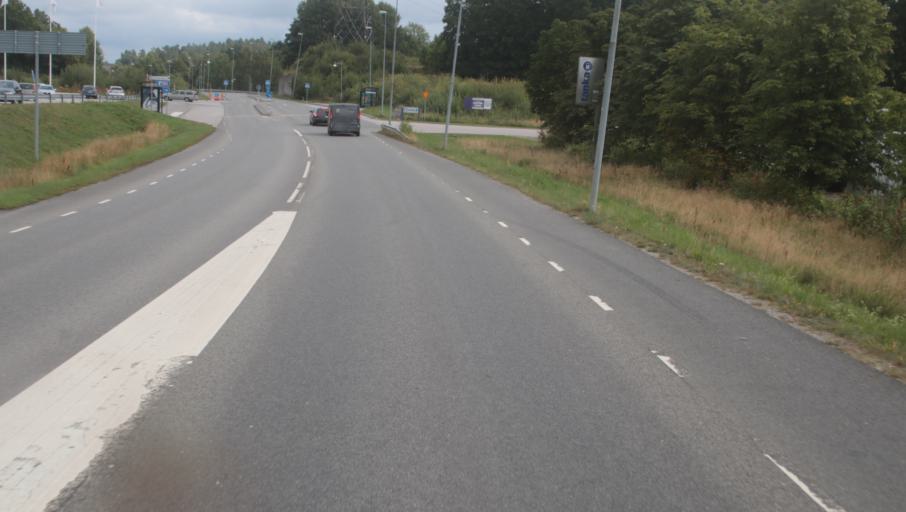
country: SE
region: Blekinge
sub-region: Karlshamns Kommun
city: Karlshamn
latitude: 56.1947
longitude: 14.8437
